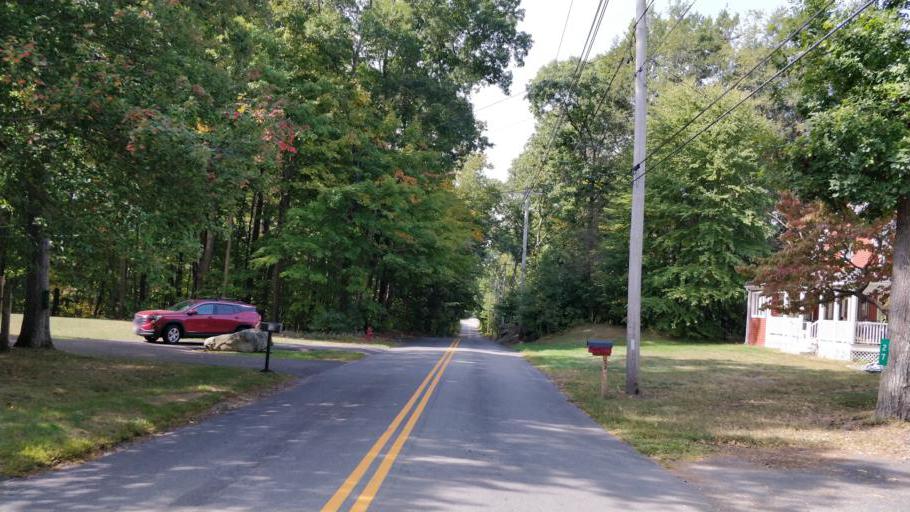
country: US
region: Massachusetts
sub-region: Bristol County
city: Norton
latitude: 41.9474
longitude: -71.2281
